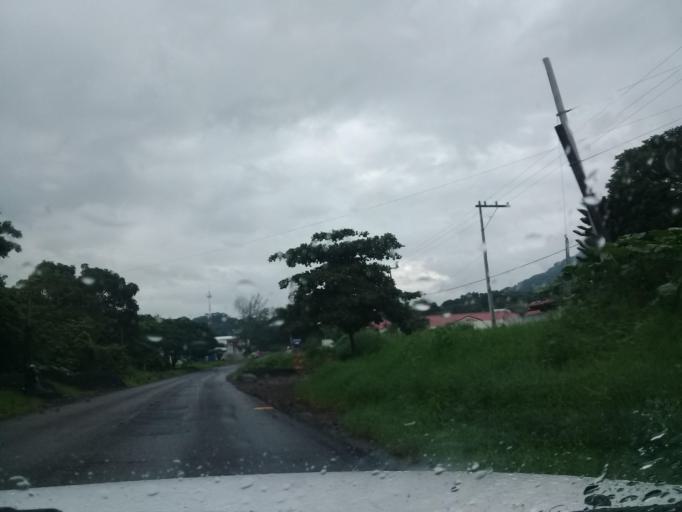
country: MX
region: Veracruz
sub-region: San Andres Tuxtla
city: Matacapan
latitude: 18.4345
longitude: -95.1893
